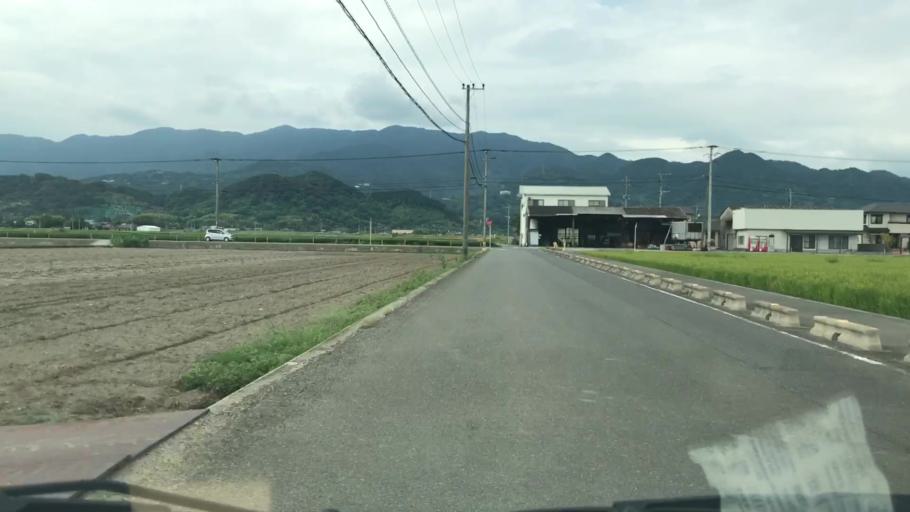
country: JP
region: Saga Prefecture
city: Saga-shi
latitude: 33.2882
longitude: 130.2248
